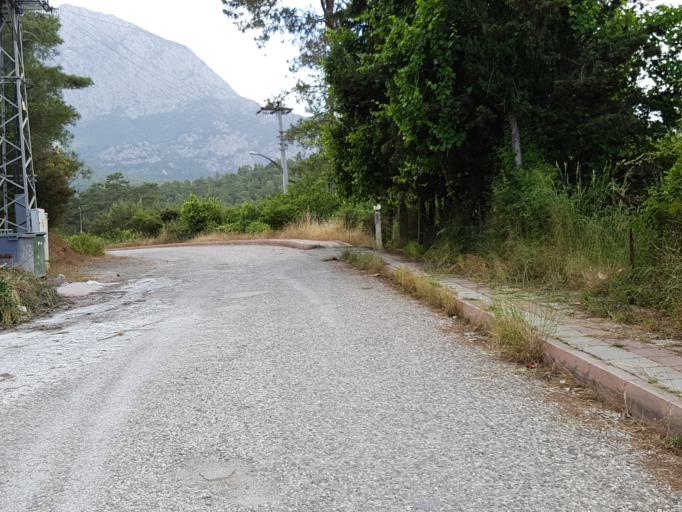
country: TR
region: Antalya
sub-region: Kemer
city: Goeynuek
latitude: 36.6437
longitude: 30.5511
